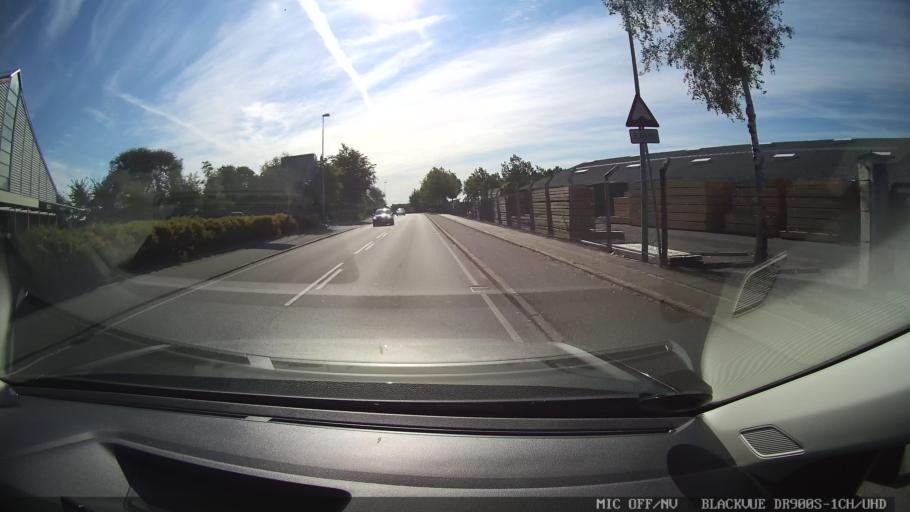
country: DK
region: North Denmark
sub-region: Mariagerfjord Kommune
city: Arden
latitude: 56.7673
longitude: 9.8633
